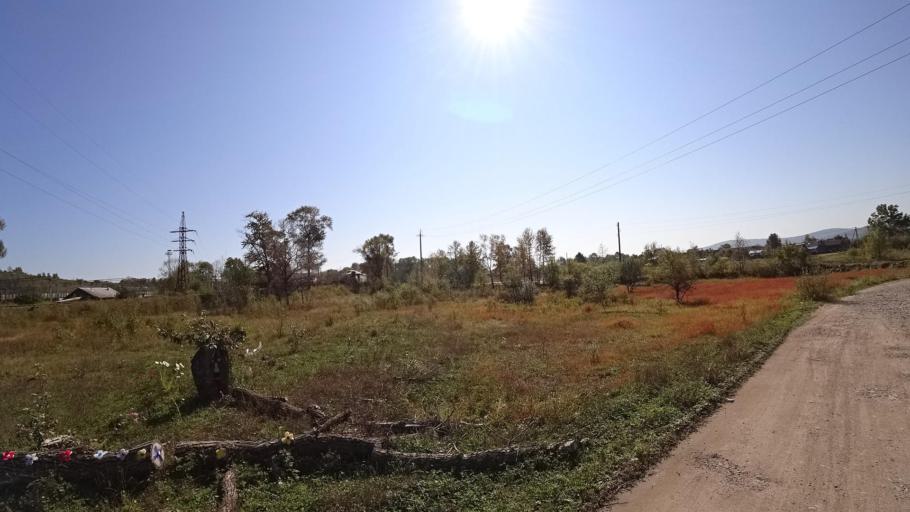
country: RU
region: Jewish Autonomous Oblast
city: Bira
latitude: 49.0012
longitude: 132.4510
